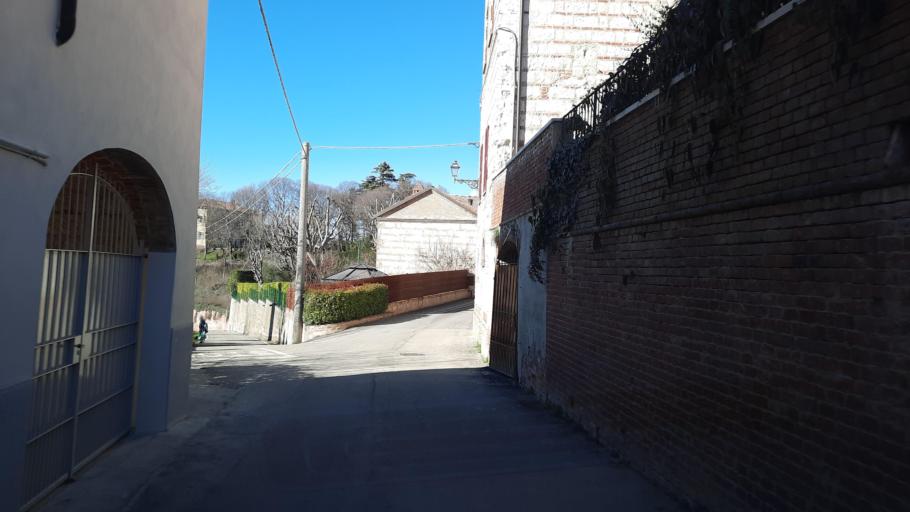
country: IT
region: Piedmont
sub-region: Provincia di Alessandria
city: Olivola
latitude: 45.0372
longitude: 8.3670
